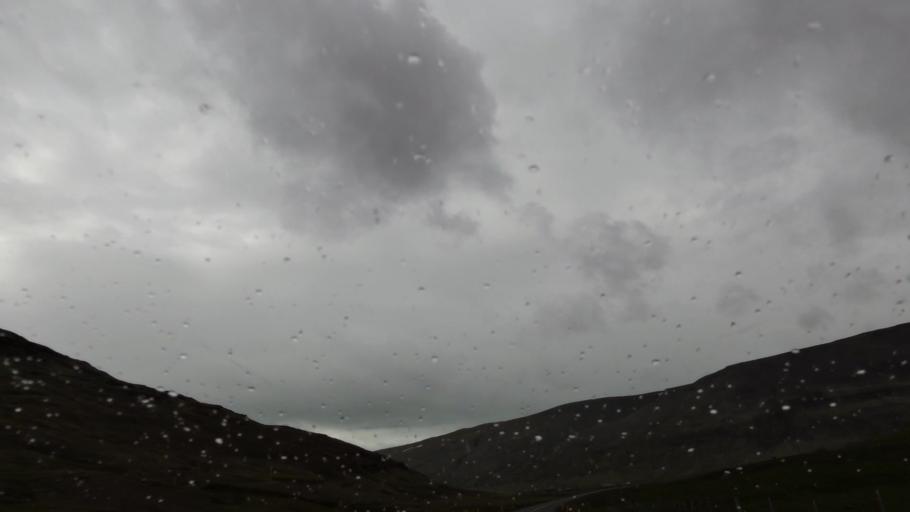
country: IS
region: West
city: Borgarnes
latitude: 65.3471
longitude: -21.7623
